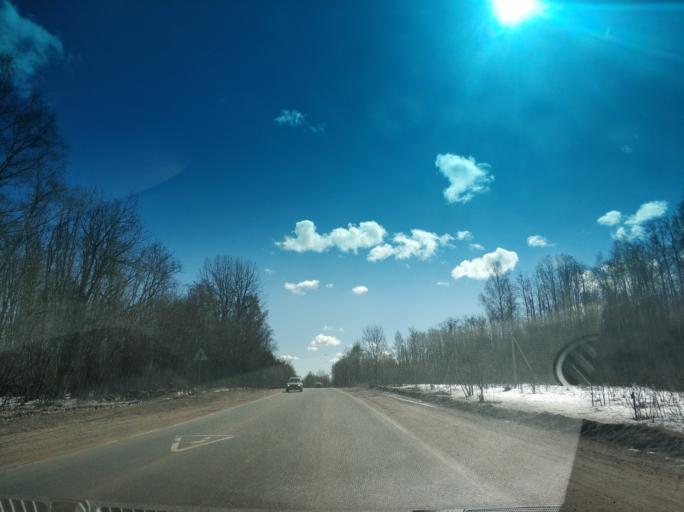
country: RU
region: Leningrad
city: Sosnovo
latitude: 60.4423
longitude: 30.2347
